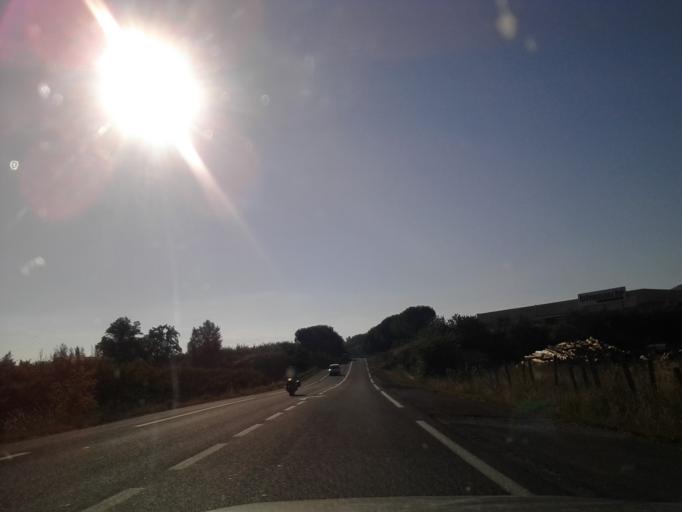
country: FR
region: Languedoc-Roussillon
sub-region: Departement des Pyrenees-Orientales
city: Prades
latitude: 42.6235
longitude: 2.4338
